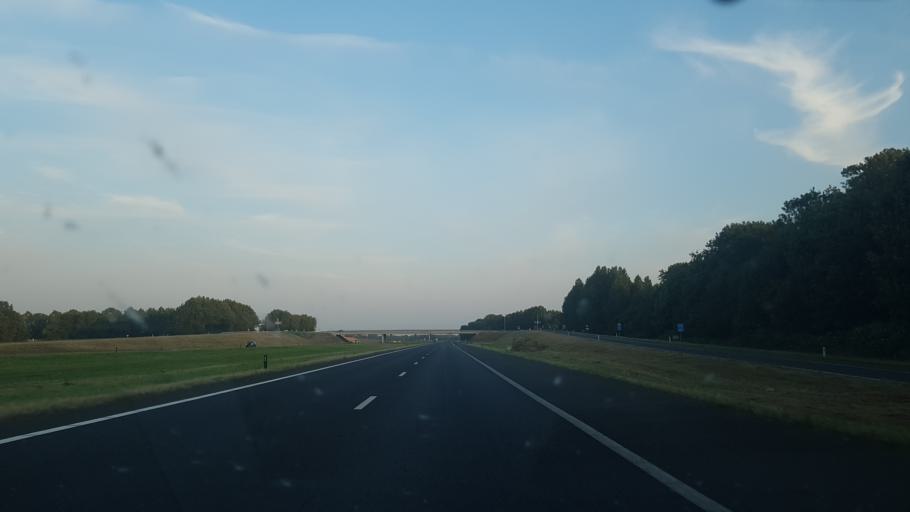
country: NL
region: Flevoland
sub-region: Gemeente Noordoostpolder
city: Emmeloord
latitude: 52.7687
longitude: 5.7627
